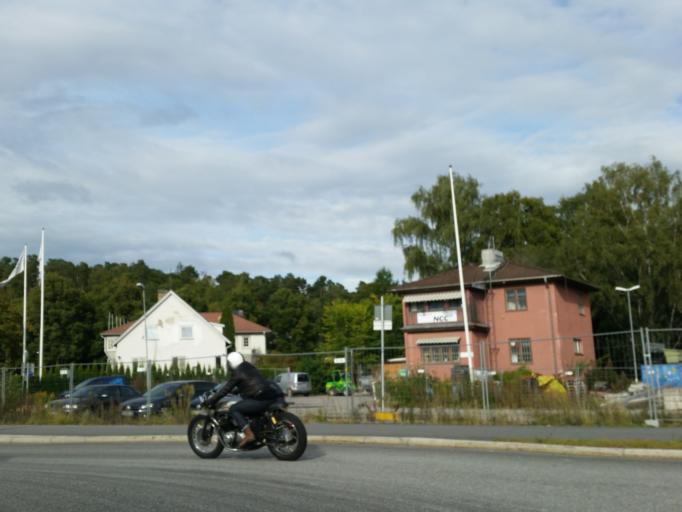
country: SE
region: Stockholm
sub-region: Sollentuna Kommun
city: Sollentuna
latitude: 59.4258
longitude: 17.9546
